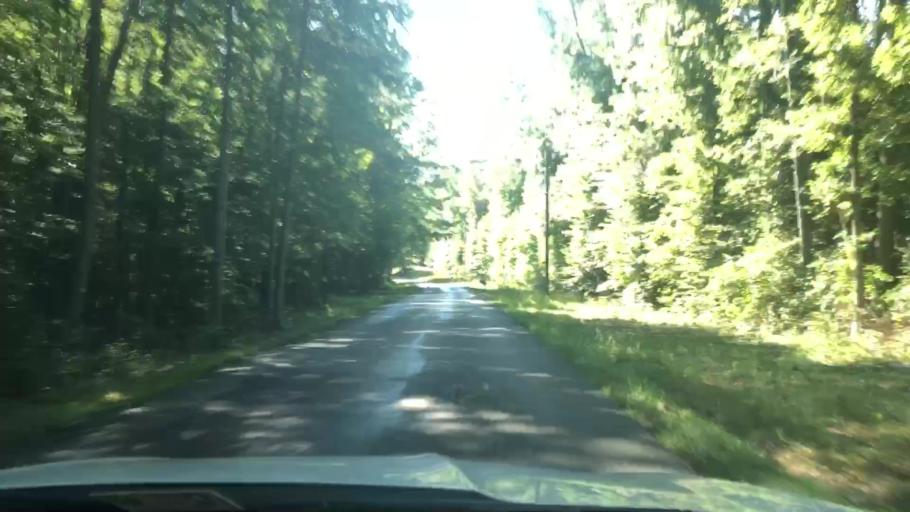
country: US
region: Virginia
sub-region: New Kent County
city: New Kent
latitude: 37.4761
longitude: -76.9330
